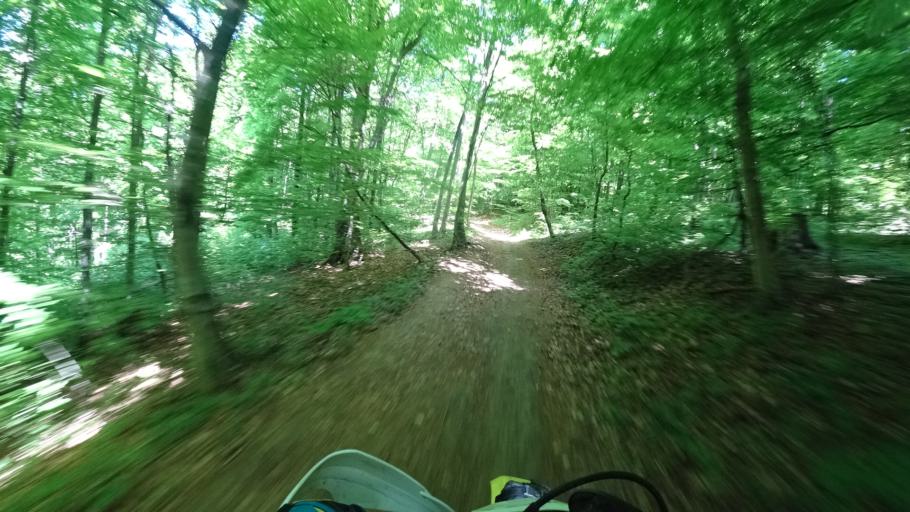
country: HR
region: Zagrebacka
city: Jablanovec
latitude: 45.8558
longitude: 15.8597
